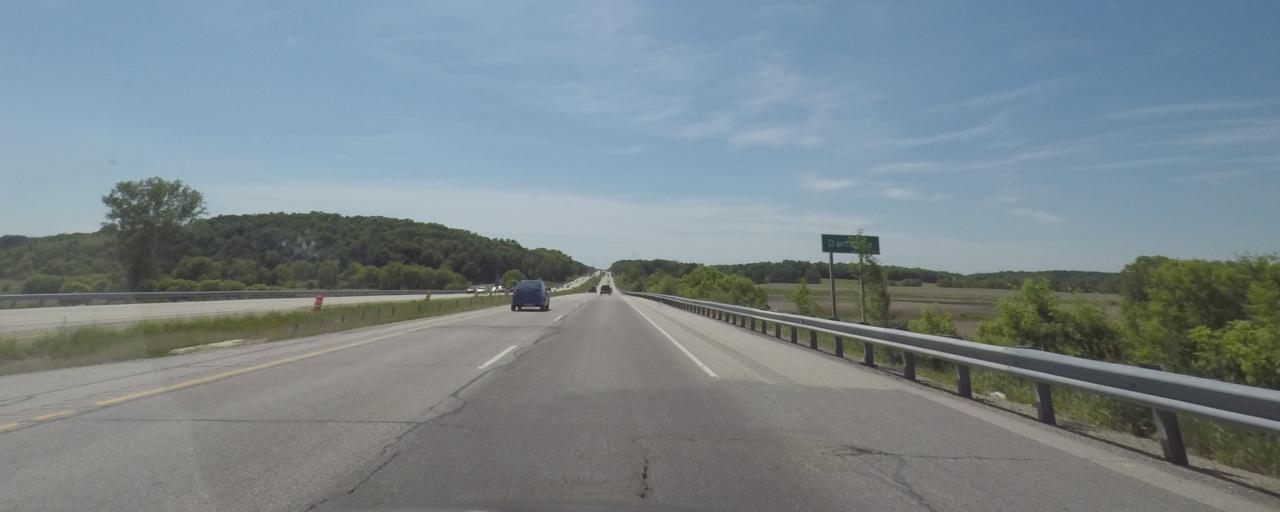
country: US
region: Wisconsin
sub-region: Jefferson County
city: Waterloo
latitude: 43.1109
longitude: -89.0118
